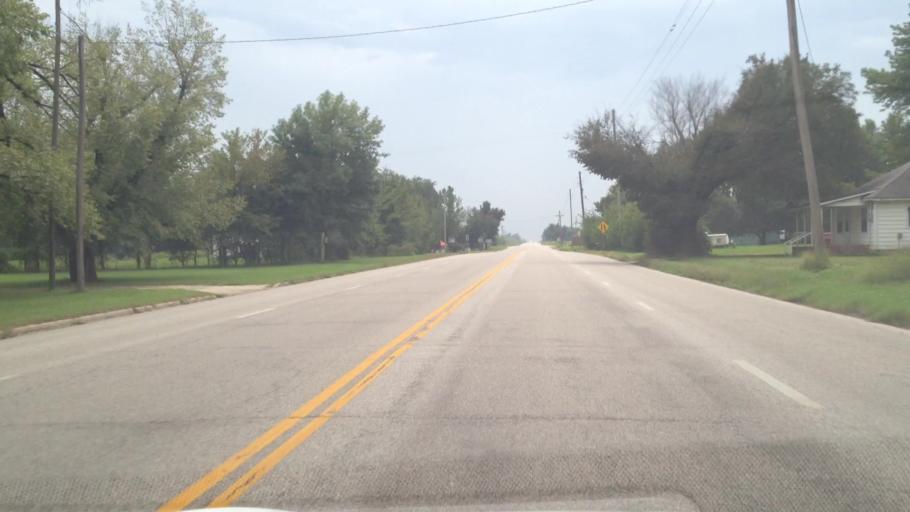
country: US
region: Kansas
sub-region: Cherokee County
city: Galena
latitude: 37.1664
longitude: -94.7044
